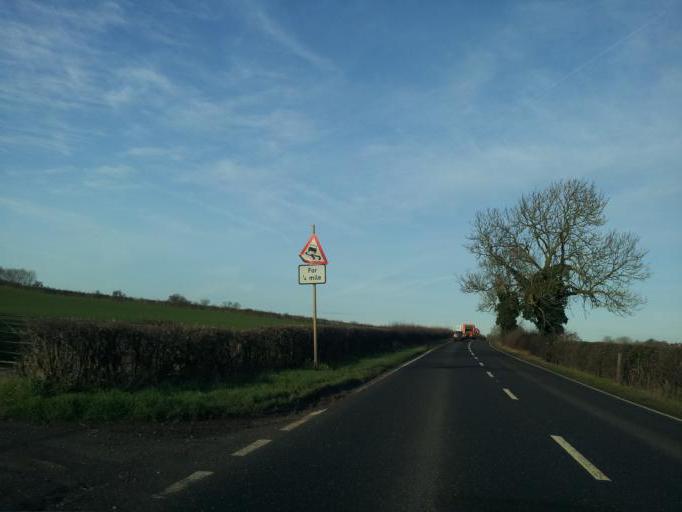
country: GB
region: England
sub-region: Nottinghamshire
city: Farndon
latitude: 53.0919
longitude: -0.8815
